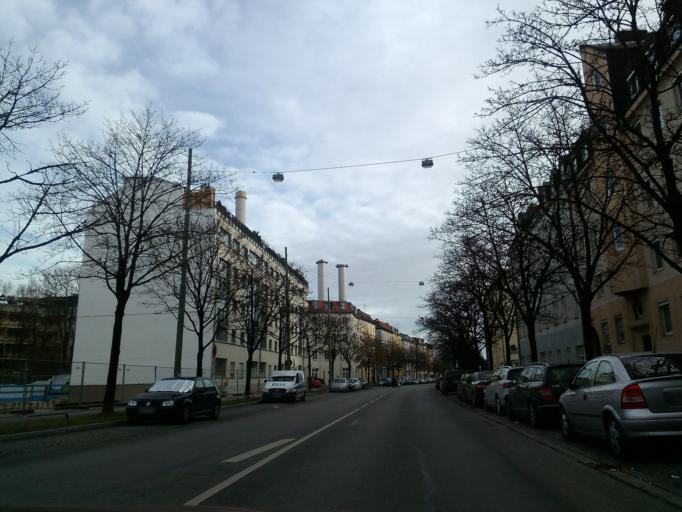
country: DE
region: Bavaria
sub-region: Upper Bavaria
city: Munich
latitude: 48.1122
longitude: 11.5496
